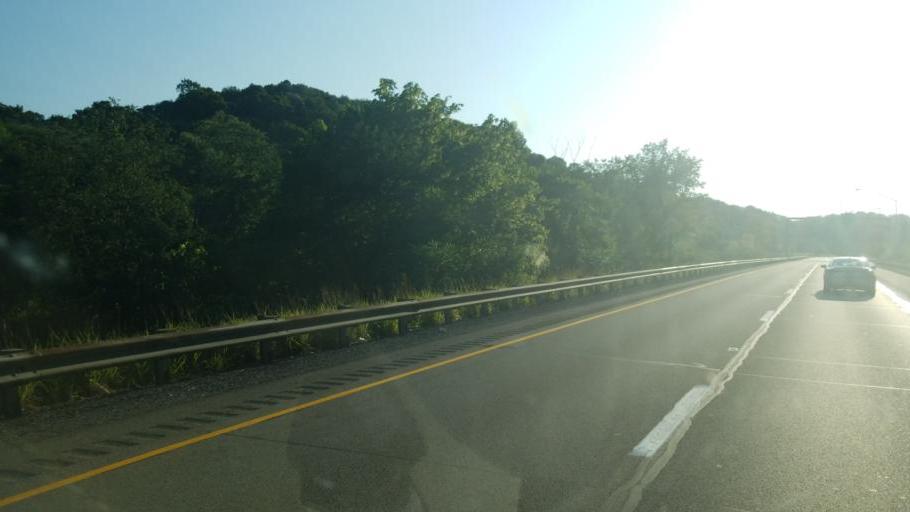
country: US
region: Pennsylvania
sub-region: Allegheny County
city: Emsworth
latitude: 40.5018
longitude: -80.1266
